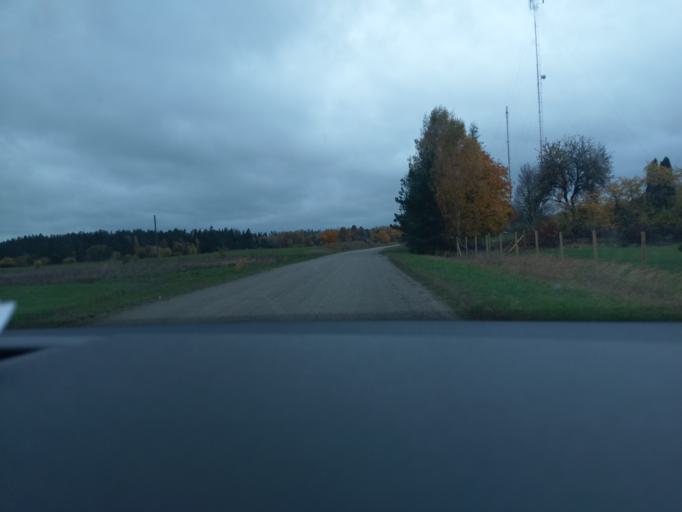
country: LV
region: Talsu Rajons
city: Stende
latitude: 57.0782
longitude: 22.2869
